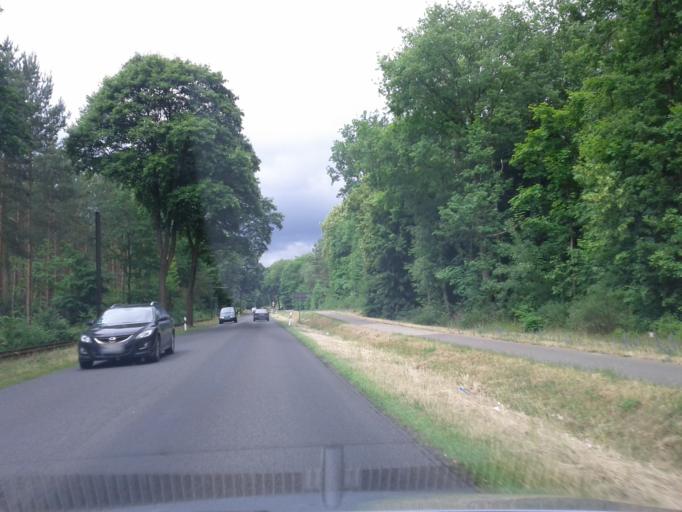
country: DE
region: Brandenburg
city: Woltersdorf
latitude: 52.4722
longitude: 13.7441
